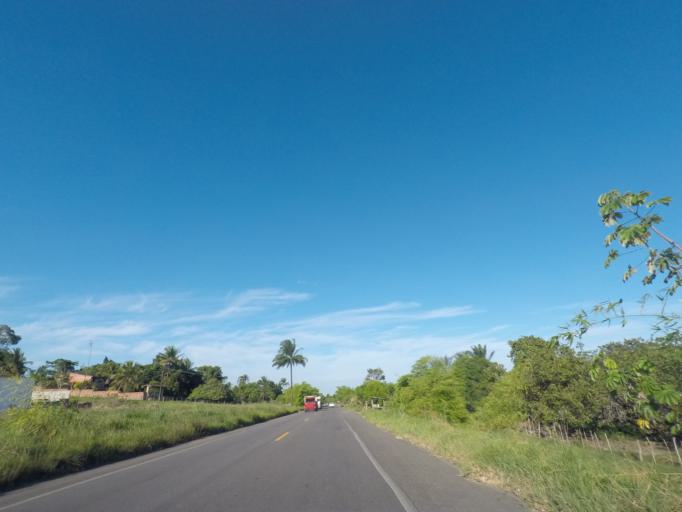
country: BR
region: Bahia
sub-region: Nazare
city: Nazare
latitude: -13.0073
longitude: -38.9686
